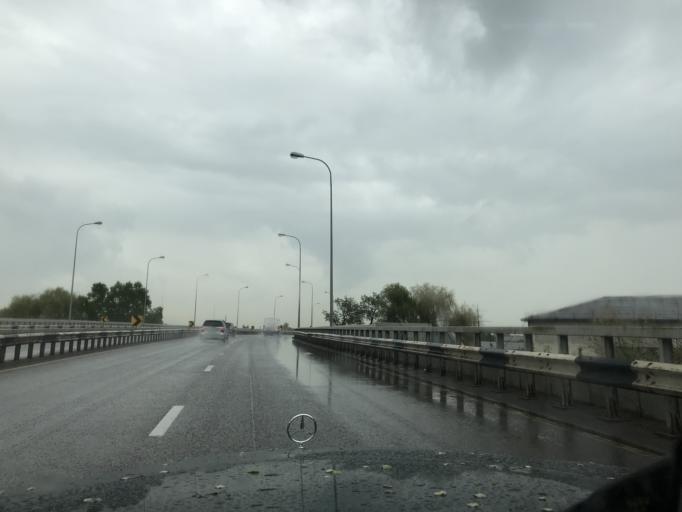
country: KZ
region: Almaty Oblysy
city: Pervomayskiy
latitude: 43.3361
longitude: 76.9633
